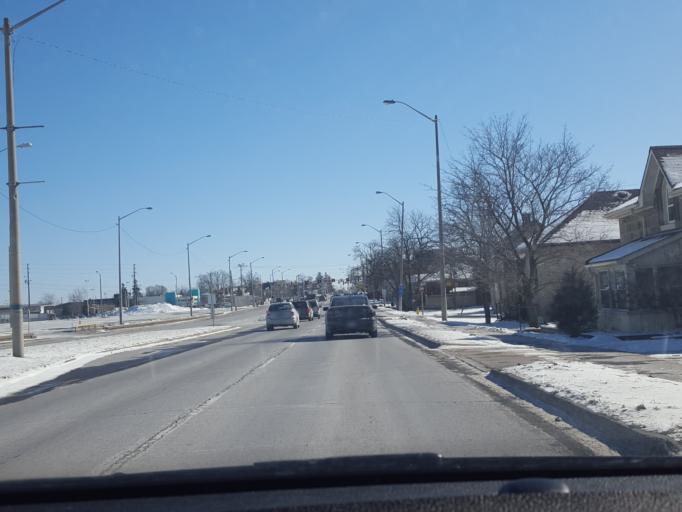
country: CA
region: Ontario
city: Cambridge
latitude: 43.3751
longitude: -80.3217
